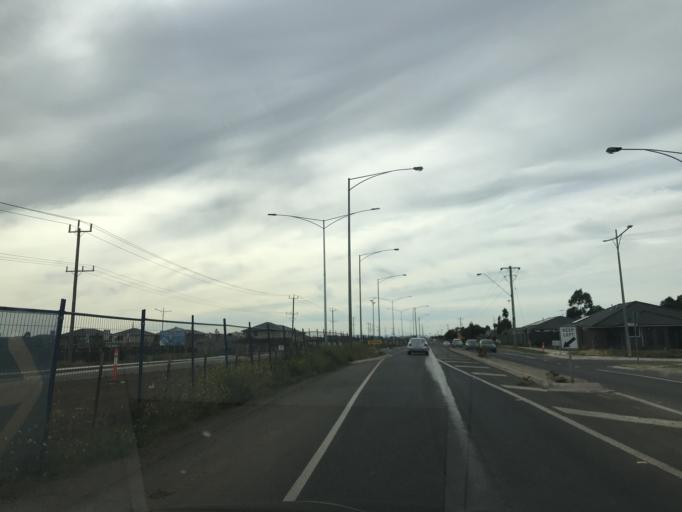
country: AU
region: Victoria
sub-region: Wyndham
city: Williams Landing
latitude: -37.8365
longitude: 144.7130
